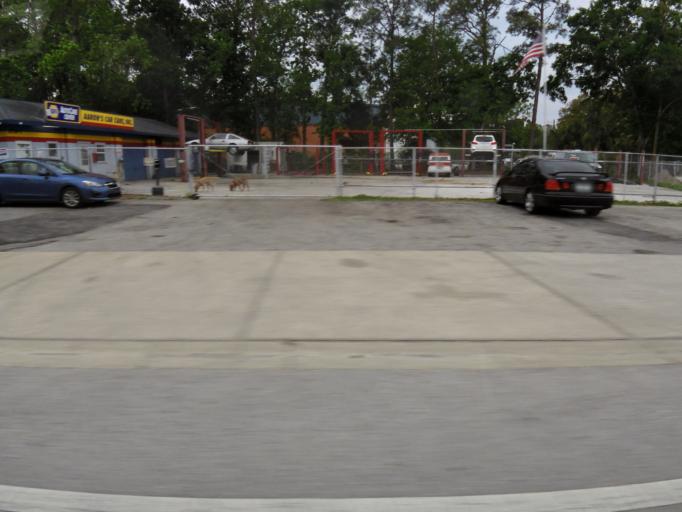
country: US
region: Florida
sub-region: Duval County
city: Jacksonville
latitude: 30.2883
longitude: -81.6248
